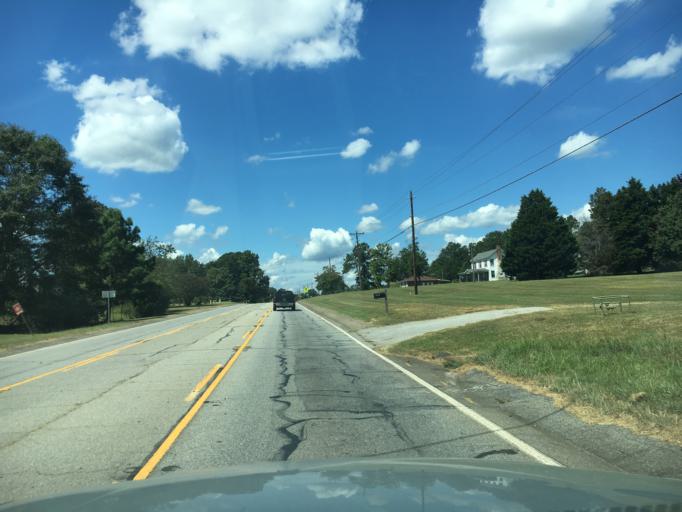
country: US
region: South Carolina
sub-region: Laurens County
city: Laurens
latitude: 34.5012
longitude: -82.0614
